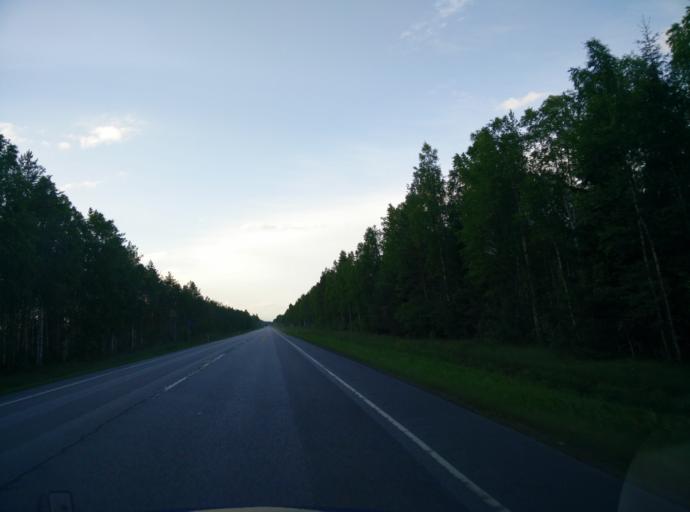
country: FI
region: Northern Ostrobothnia
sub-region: Haapavesi-Siikalatva
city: Pulkkila
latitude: 64.1304
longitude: 25.8001
